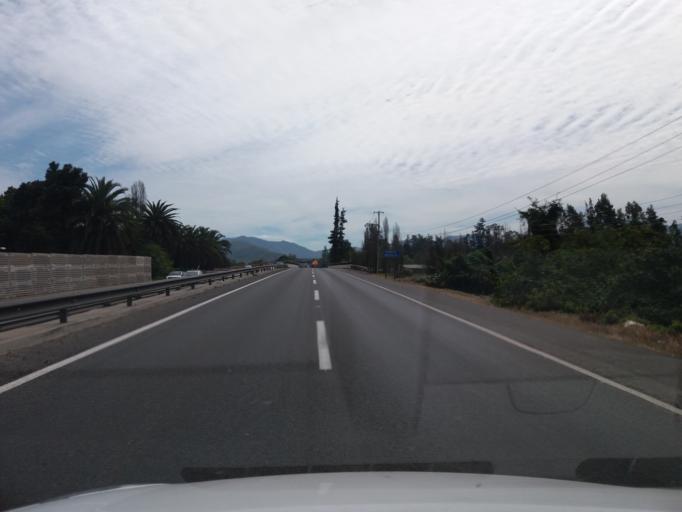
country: CL
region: Valparaiso
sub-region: Provincia de Quillota
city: Hacienda La Calera
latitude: -32.7344
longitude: -71.2001
